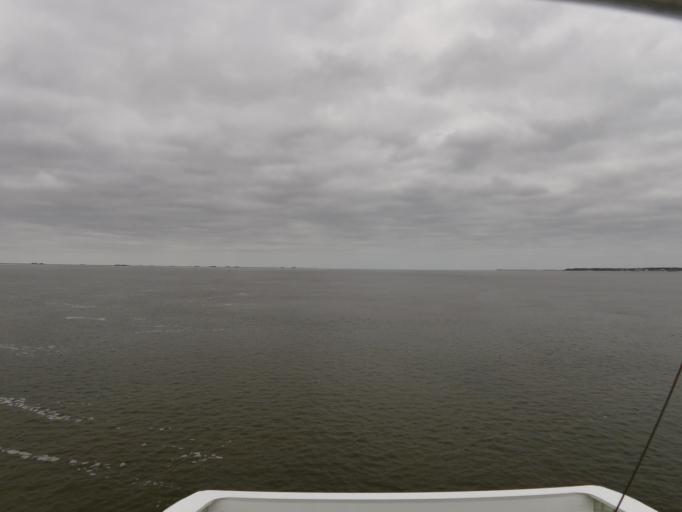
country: DE
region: Schleswig-Holstein
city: Wyk auf Fohr
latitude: 54.6938
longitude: 8.6281
